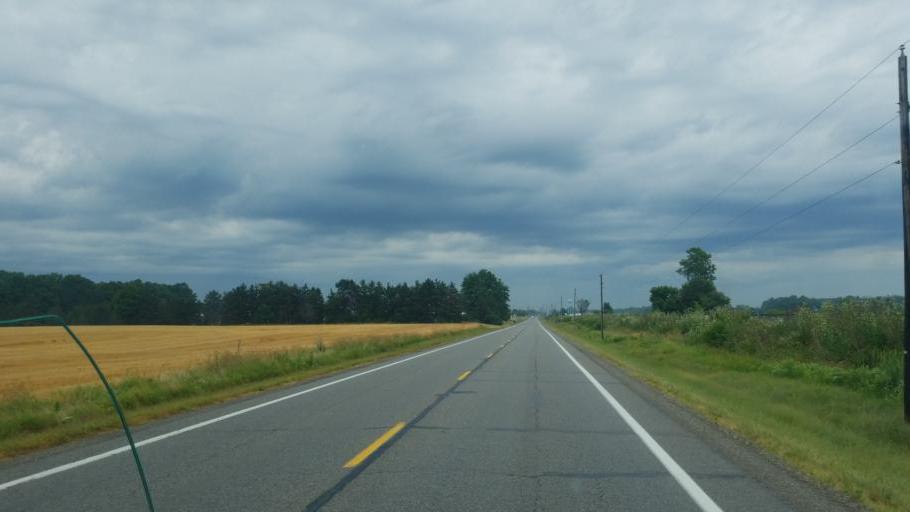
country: US
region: Ohio
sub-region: Williams County
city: Edgerton
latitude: 41.4434
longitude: -84.7755
